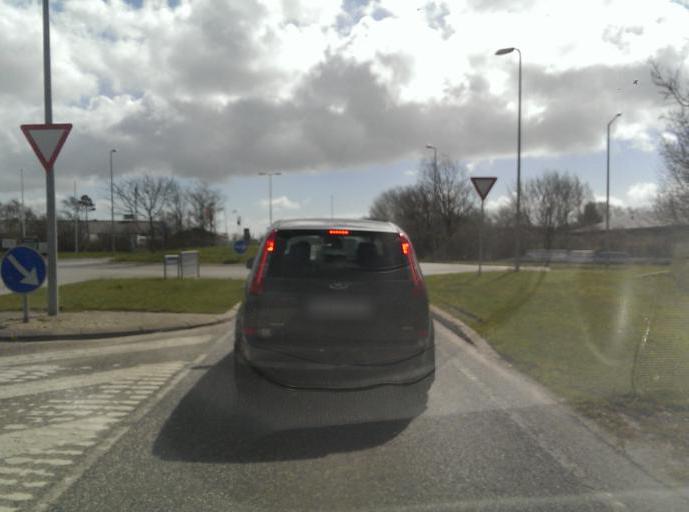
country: DK
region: South Denmark
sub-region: Esbjerg Kommune
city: Esbjerg
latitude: 55.5106
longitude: 8.4057
